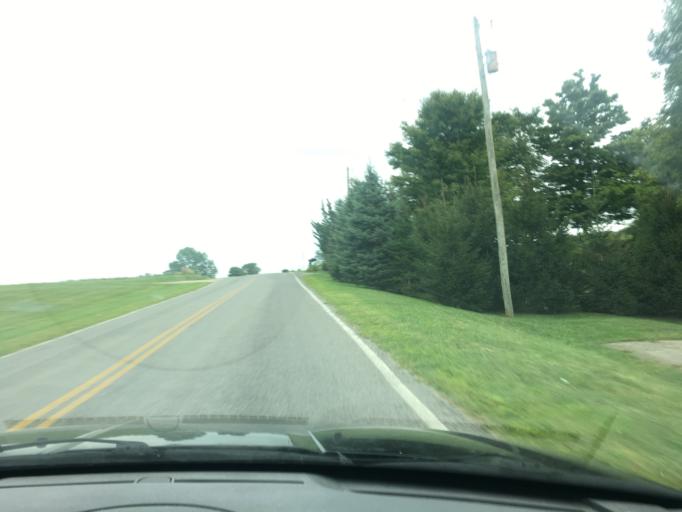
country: US
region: Ohio
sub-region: Logan County
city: West Liberty
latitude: 40.1930
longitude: -83.7695
